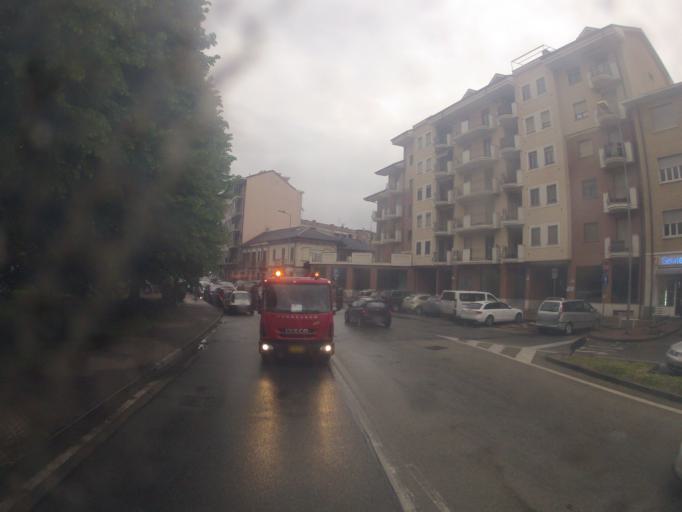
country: IT
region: Piedmont
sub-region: Provincia di Torino
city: Moncalieri
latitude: 44.9994
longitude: 7.6718
